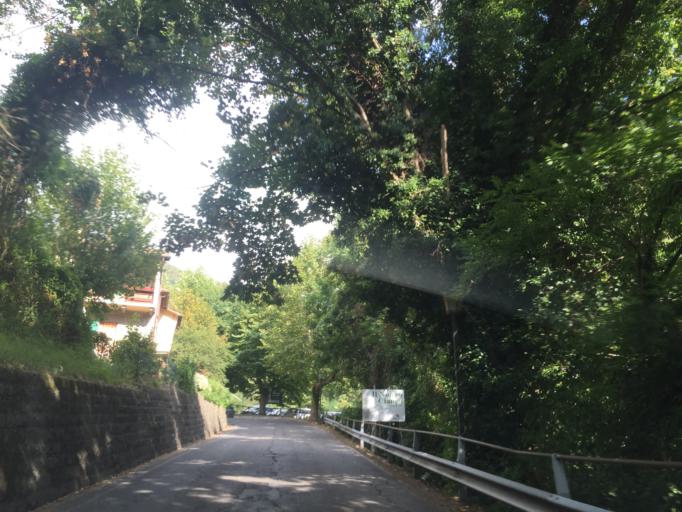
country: IT
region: Tuscany
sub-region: Provincia di Pistoia
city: Cutigliano
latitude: 44.0988
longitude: 10.7530
